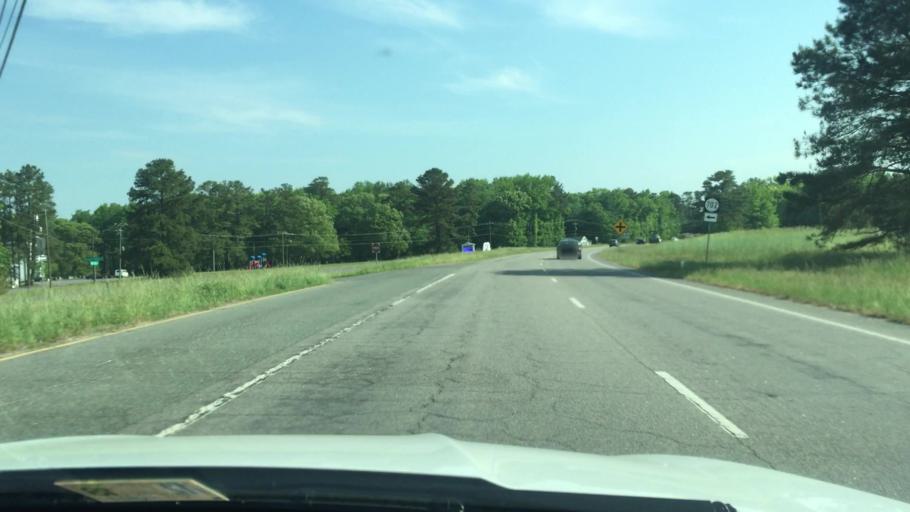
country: US
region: Virginia
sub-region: Lancaster County
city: Kilmarnock
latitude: 37.6573
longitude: -76.3885
